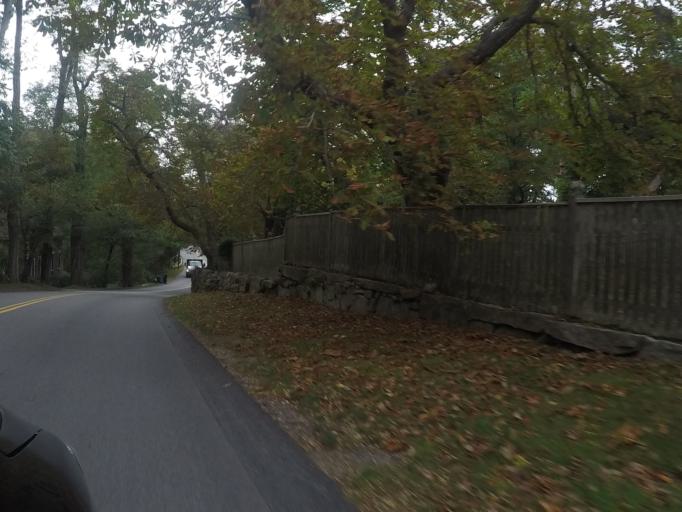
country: US
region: Massachusetts
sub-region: Bristol County
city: Smith Mills
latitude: 41.5700
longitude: -71.0041
